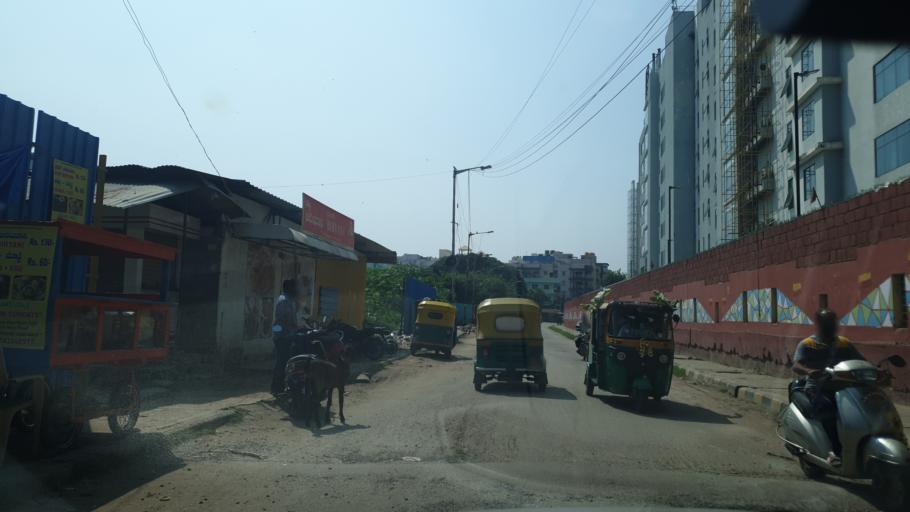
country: IN
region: Karnataka
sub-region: Bangalore Urban
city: Bangalore
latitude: 12.9795
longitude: 77.6662
